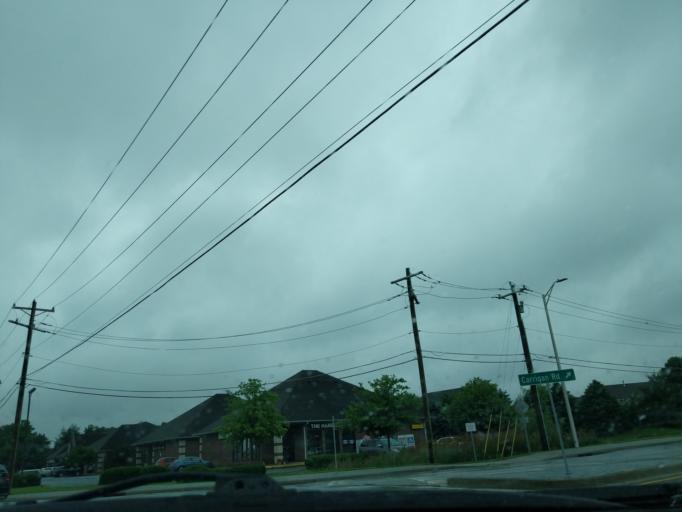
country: US
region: Indiana
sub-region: Hamilton County
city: Cicero
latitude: 40.0908
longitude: -86.0335
